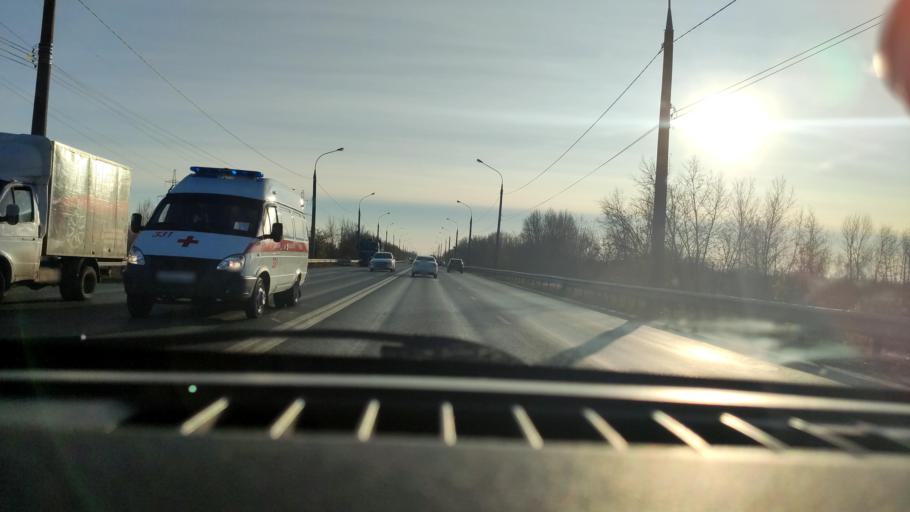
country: RU
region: Samara
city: Samara
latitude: 53.1560
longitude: 50.1902
